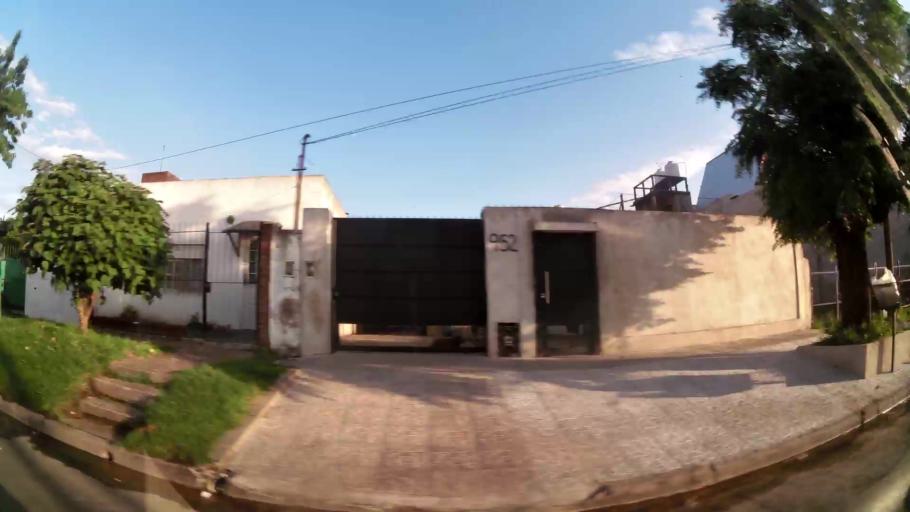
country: AR
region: Buenos Aires
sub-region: Partido de Tigre
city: Tigre
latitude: -34.4542
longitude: -58.6403
